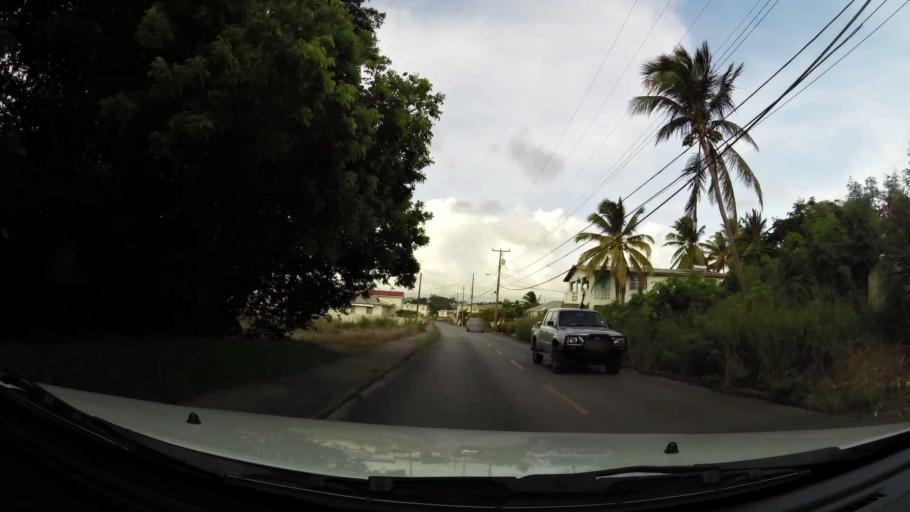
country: BB
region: Christ Church
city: Oistins
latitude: 13.0593
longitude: -59.5374
